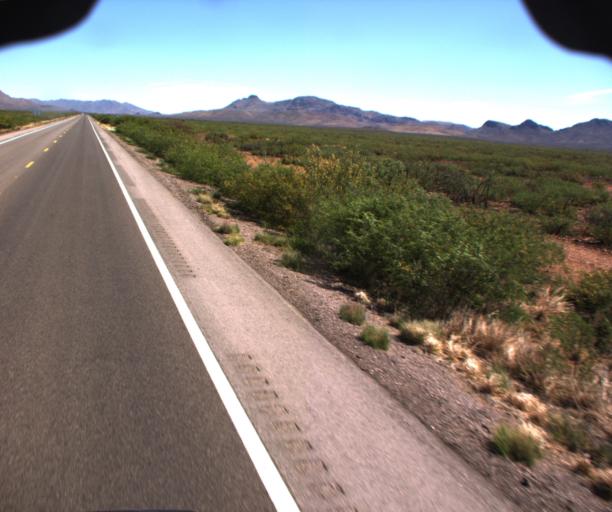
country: US
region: Arizona
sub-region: Cochise County
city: Douglas
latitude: 31.3952
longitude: -109.5083
